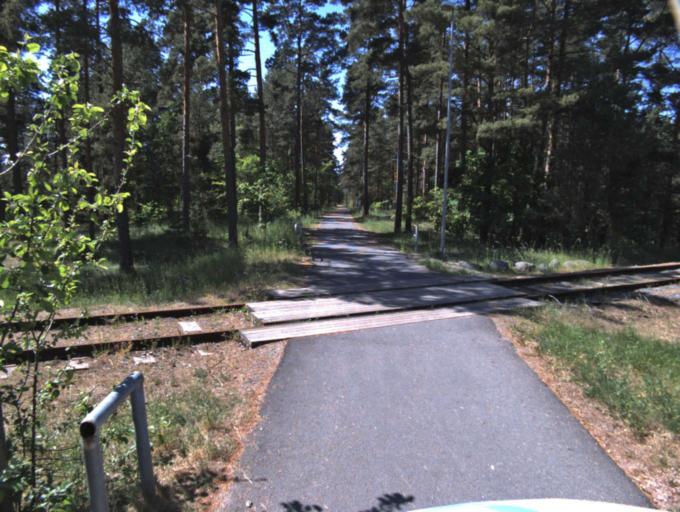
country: SE
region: Skane
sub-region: Kristianstads Kommun
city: Ahus
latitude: 55.9409
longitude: 14.2896
